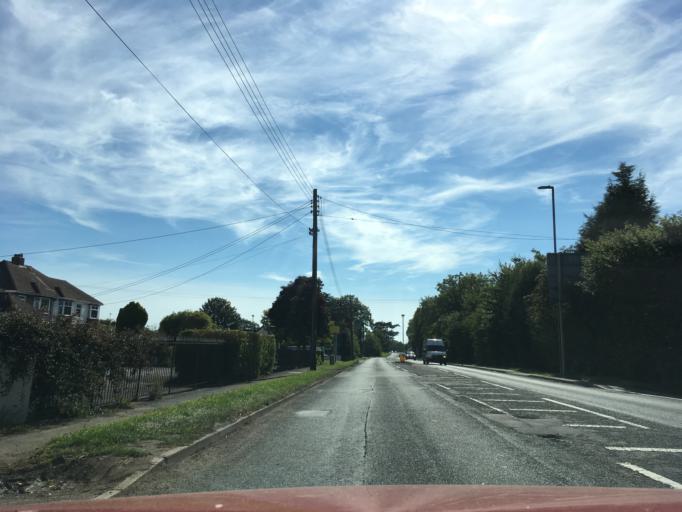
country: GB
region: England
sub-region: South Gloucestershire
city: Alveston
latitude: 51.5758
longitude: -2.5424
